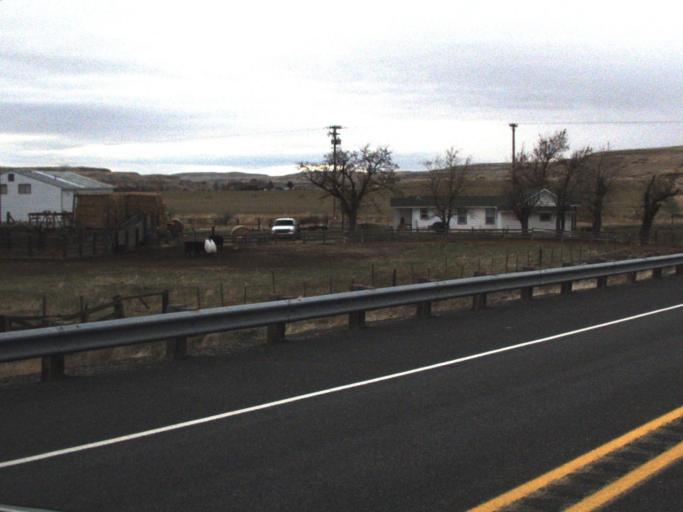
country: US
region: Washington
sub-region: Columbia County
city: Dayton
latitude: 46.7724
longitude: -118.0388
